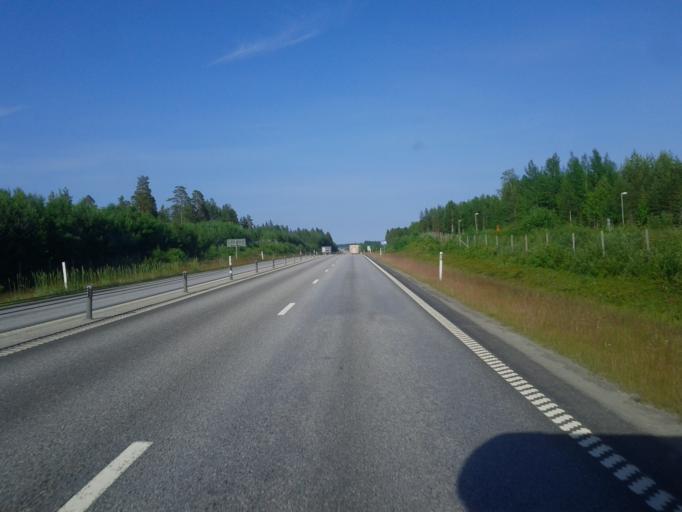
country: SE
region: Vaesterbotten
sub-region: Umea Kommun
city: Ersmark
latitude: 63.8506
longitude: 20.3631
